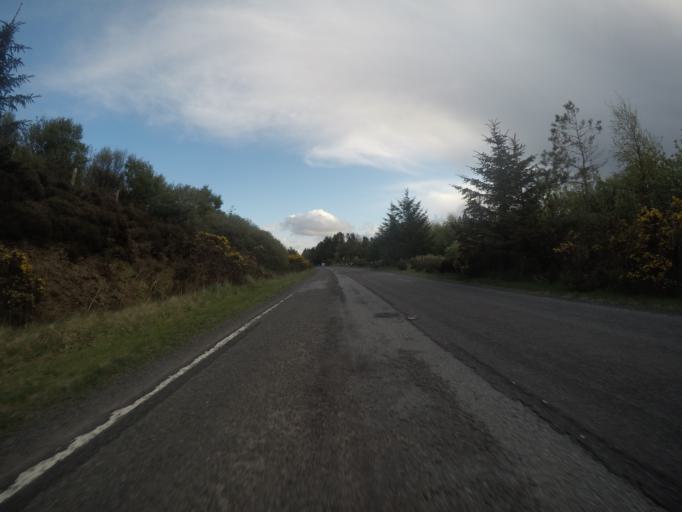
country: GB
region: Scotland
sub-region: Highland
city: Portree
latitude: 57.5708
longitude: -6.3642
